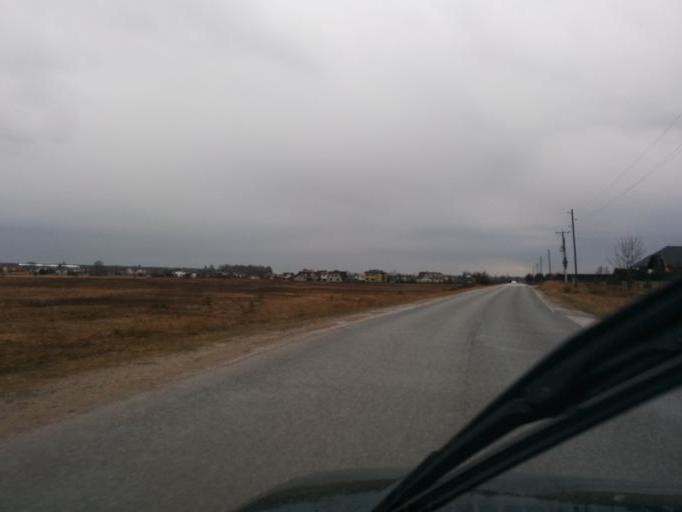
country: LV
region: Kekava
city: Balozi
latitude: 56.8940
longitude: 24.1756
